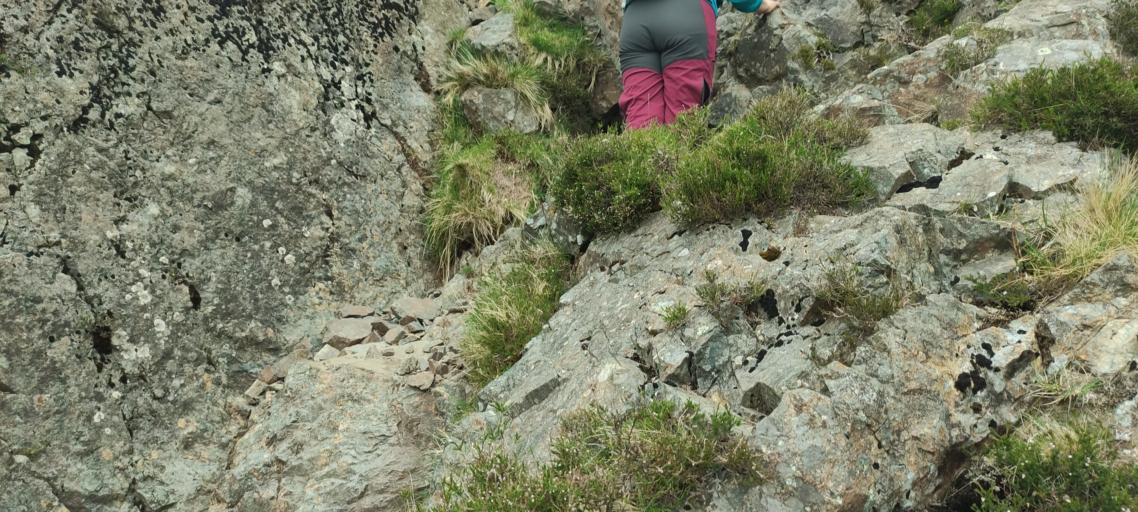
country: GB
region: England
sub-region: Cumbria
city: Keswick
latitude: 54.4579
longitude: -3.2823
